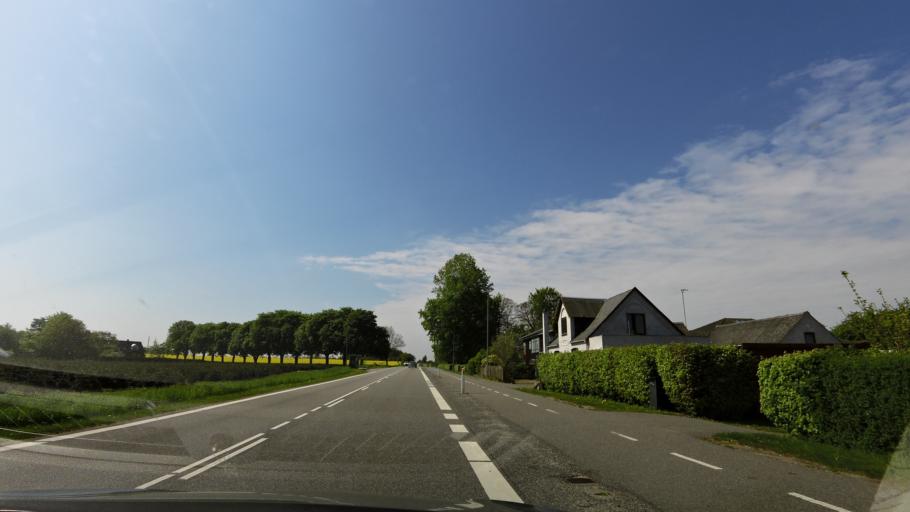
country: DK
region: South Denmark
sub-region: Nyborg Kommune
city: Ullerslev
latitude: 55.2807
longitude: 10.6880
